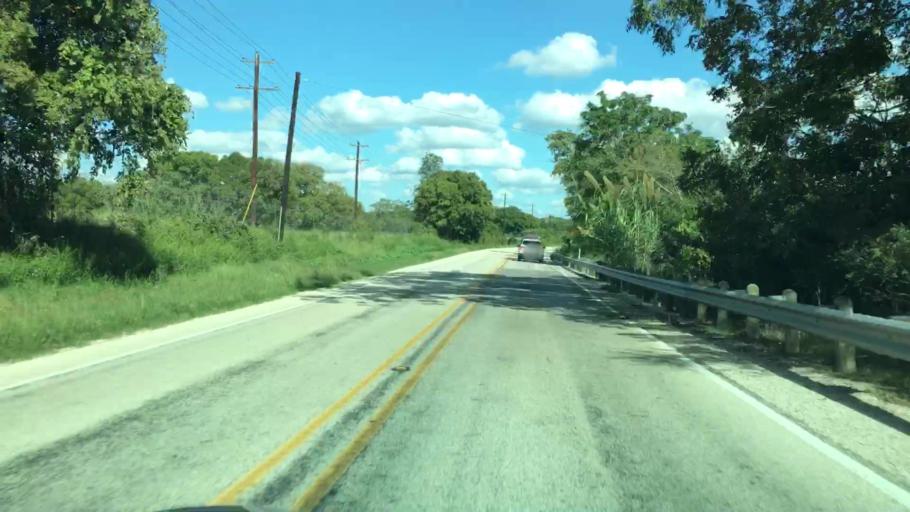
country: US
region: Texas
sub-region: Blanco County
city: Blanco
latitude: 30.0914
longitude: -98.3808
